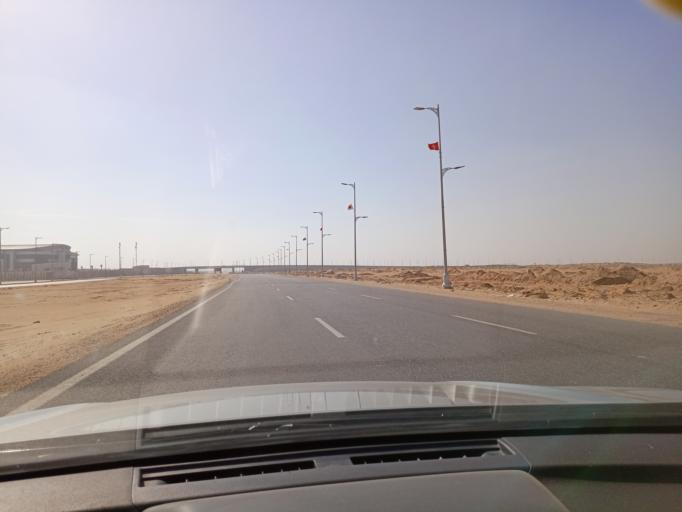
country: EG
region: Muhafazat al Qalyubiyah
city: Al Khankah
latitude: 30.0444
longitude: 31.6939
